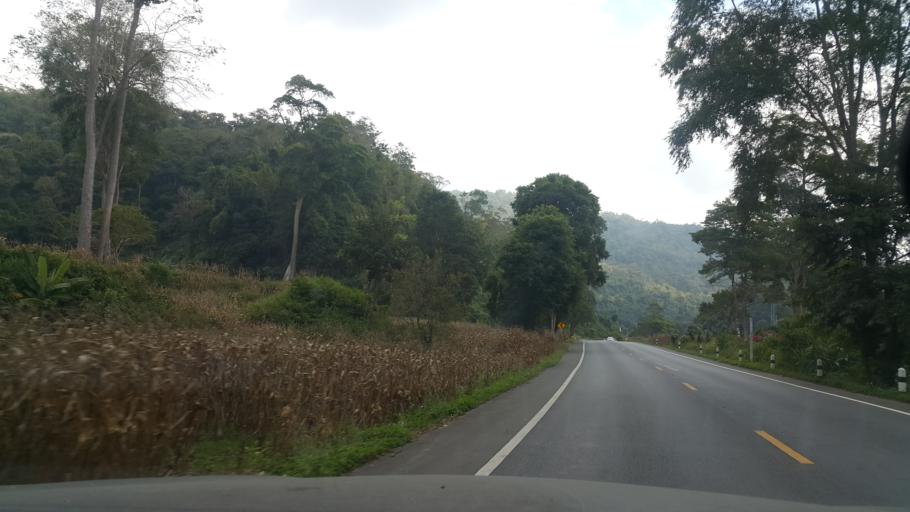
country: TH
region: Lampang
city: Wang Nuea
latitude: 19.0644
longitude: 99.7470
